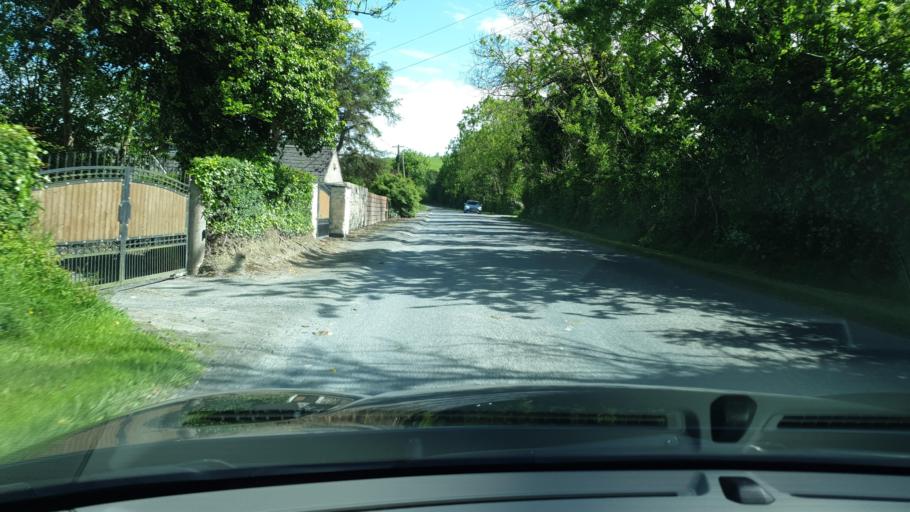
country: IE
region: Leinster
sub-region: An Mhi
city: Slane
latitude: 53.7671
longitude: -6.6206
